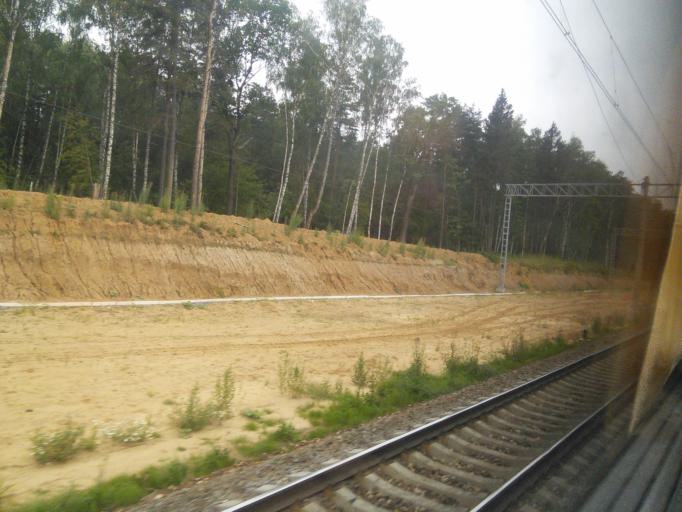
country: RU
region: Moskovskaya
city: Novoivanovskoye
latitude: 55.7030
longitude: 37.3469
